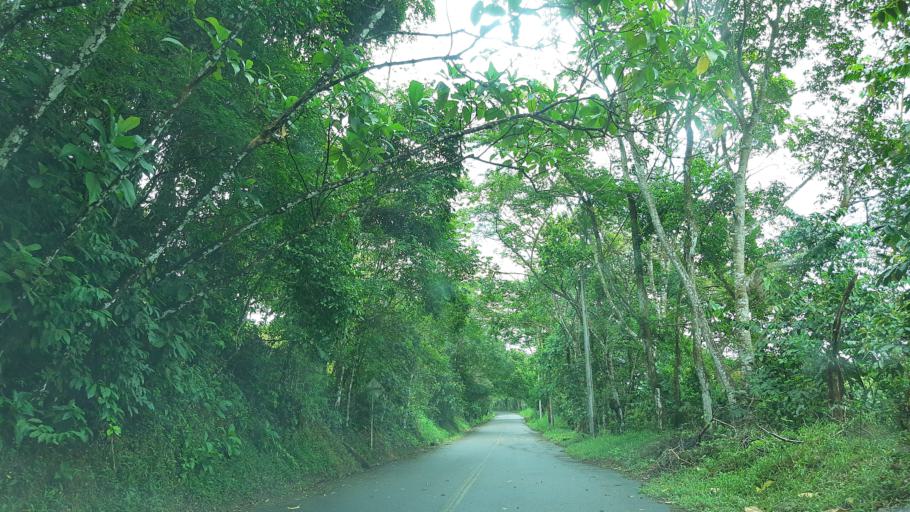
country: CO
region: Casanare
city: Sabanalarga
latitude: 4.8191
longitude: -73.0694
